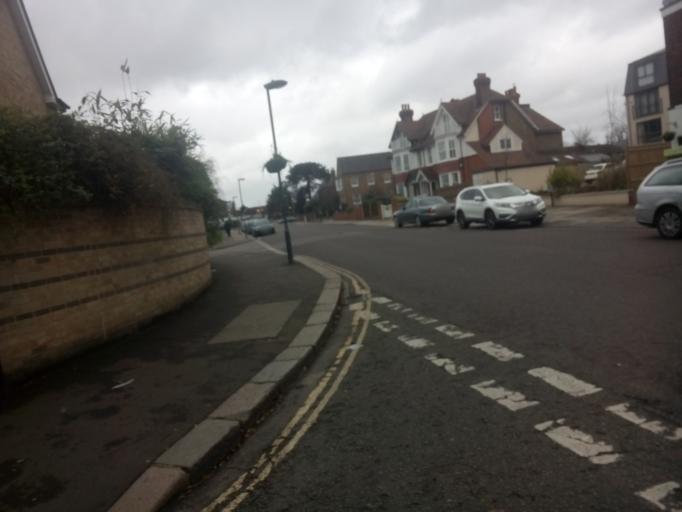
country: GB
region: England
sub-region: Greater London
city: Hampton
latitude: 51.4152
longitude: -0.3675
